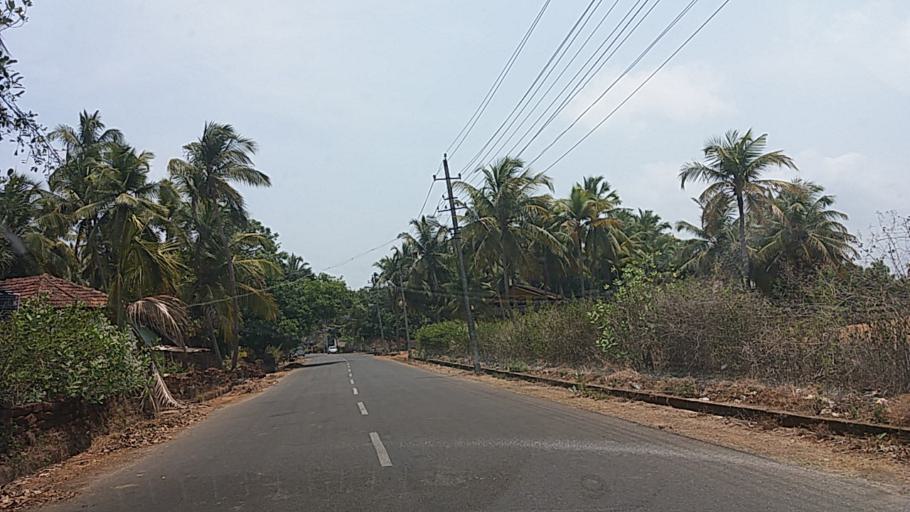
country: IN
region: Karnataka
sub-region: Uttar Kannada
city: Karwar
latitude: 14.8166
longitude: 74.1508
